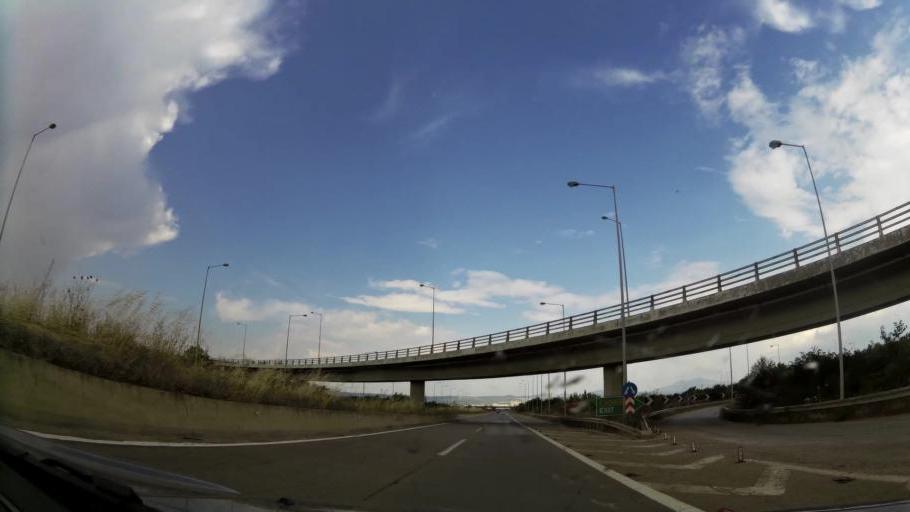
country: GR
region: Central Macedonia
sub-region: Nomos Thessalonikis
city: Kalochori
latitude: 40.6532
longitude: 22.8425
